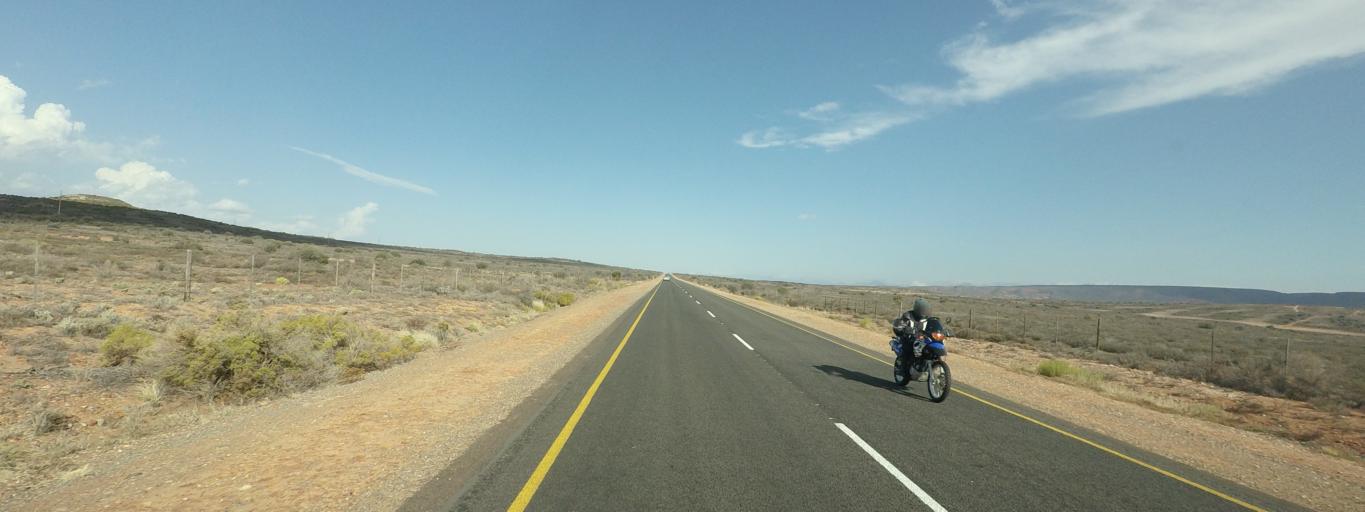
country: ZA
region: Western Cape
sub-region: Eden District Municipality
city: Oudtshoorn
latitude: -33.5849
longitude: 21.9836
